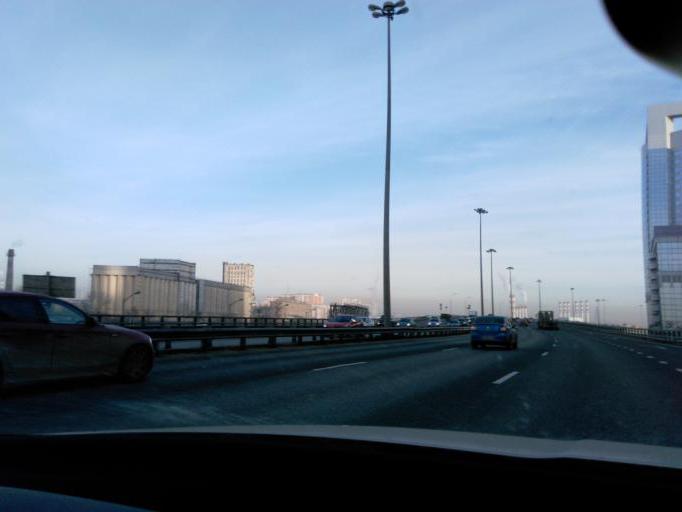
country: RU
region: Moskovskaya
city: Presnenskiy
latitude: 55.7492
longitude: 37.5324
